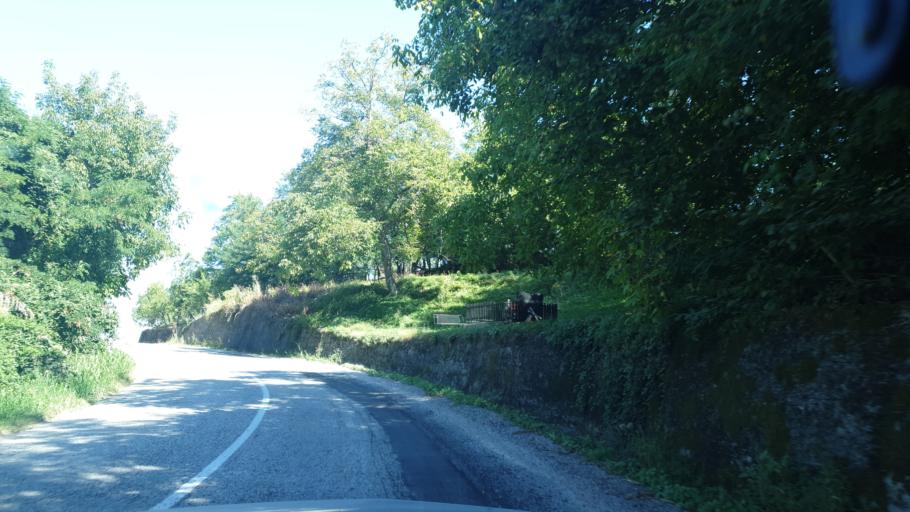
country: RS
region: Central Serbia
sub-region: Kolubarski Okrug
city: Mionica
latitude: 44.1555
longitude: 19.9908
